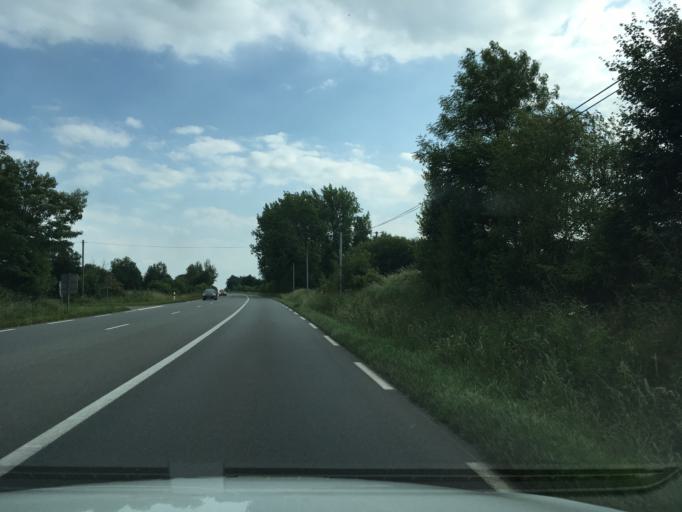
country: FR
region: Poitou-Charentes
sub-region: Departement des Deux-Sevres
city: Le Tallud
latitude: 46.6201
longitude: -0.2820
